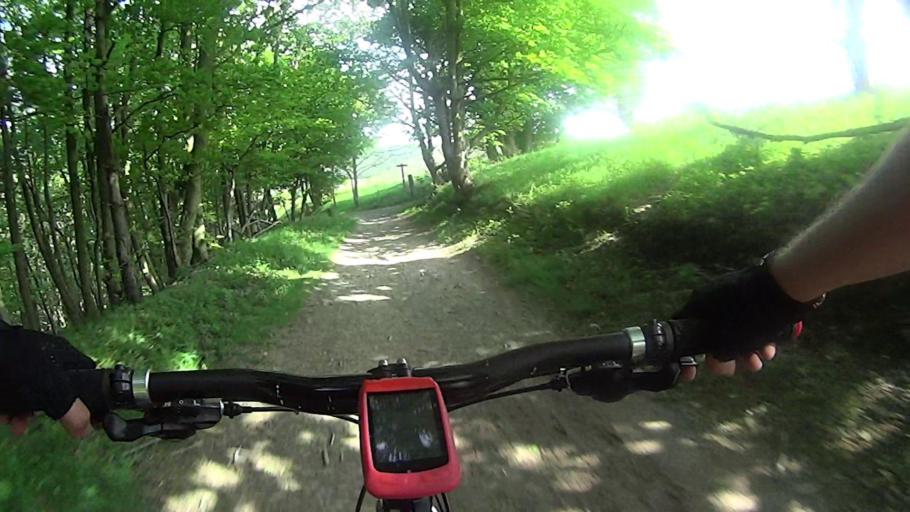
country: GB
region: England
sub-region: West Sussex
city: Milland
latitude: 50.9588
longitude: -0.8395
